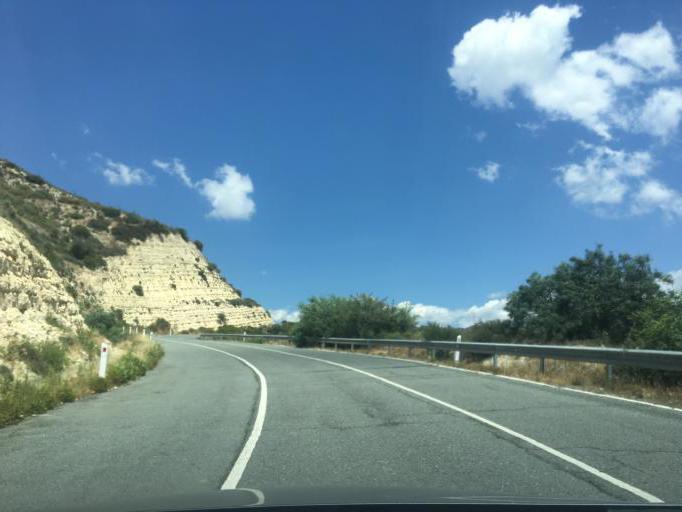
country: CY
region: Limassol
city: Mouttagiaka
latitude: 34.7607
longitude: 33.0627
